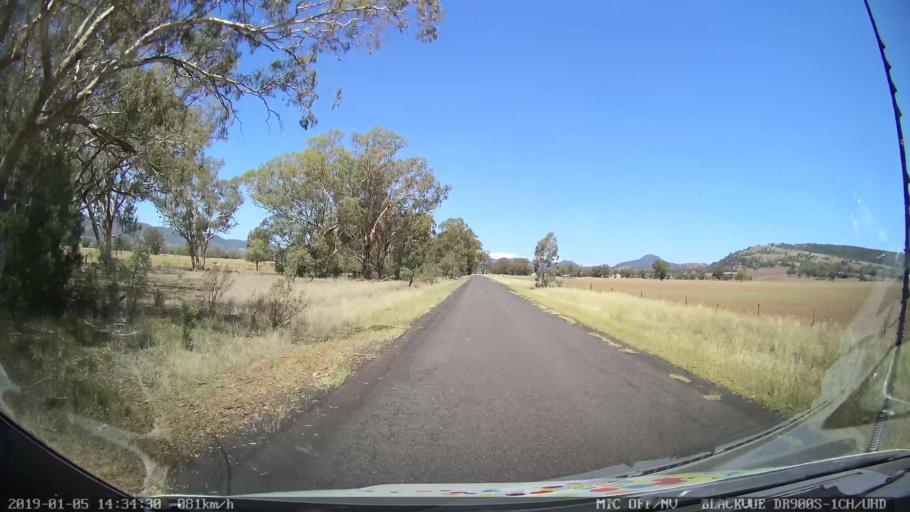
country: AU
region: New South Wales
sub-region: Tamworth Municipality
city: Phillip
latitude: -31.2334
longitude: 150.6423
